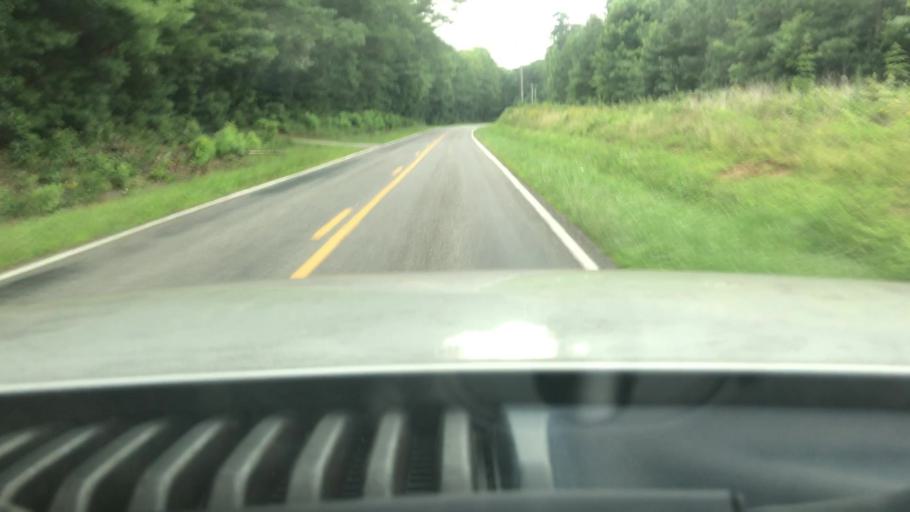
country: US
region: North Carolina
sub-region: Surry County
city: Dobson
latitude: 36.4115
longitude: -80.8177
